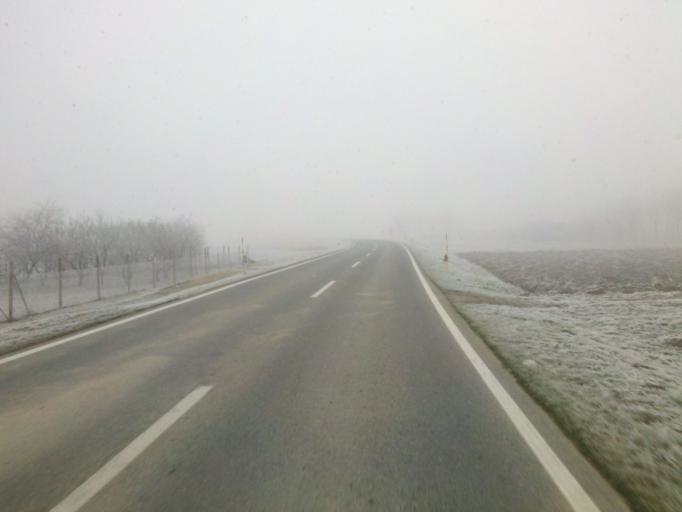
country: HR
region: Medimurska
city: Ivanovec
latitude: 46.3695
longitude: 16.4874
